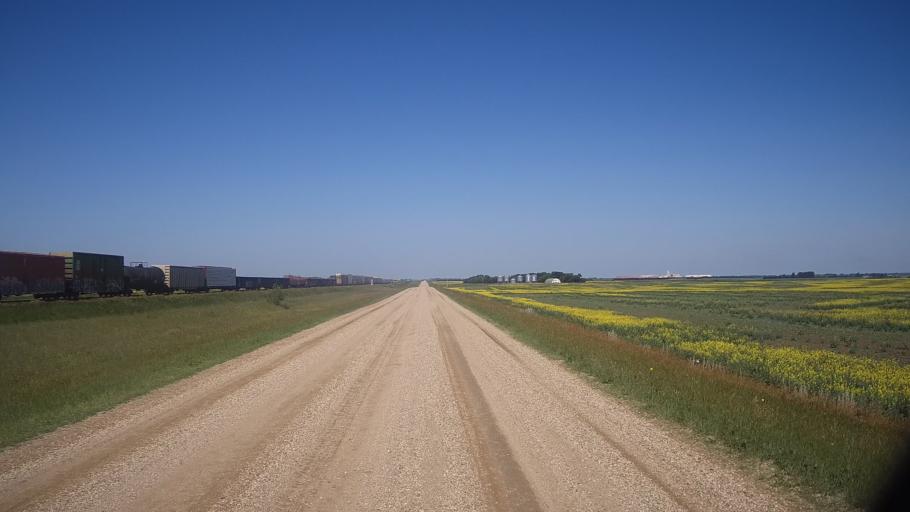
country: CA
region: Saskatchewan
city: Watrous
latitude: 51.8598
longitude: -105.9611
